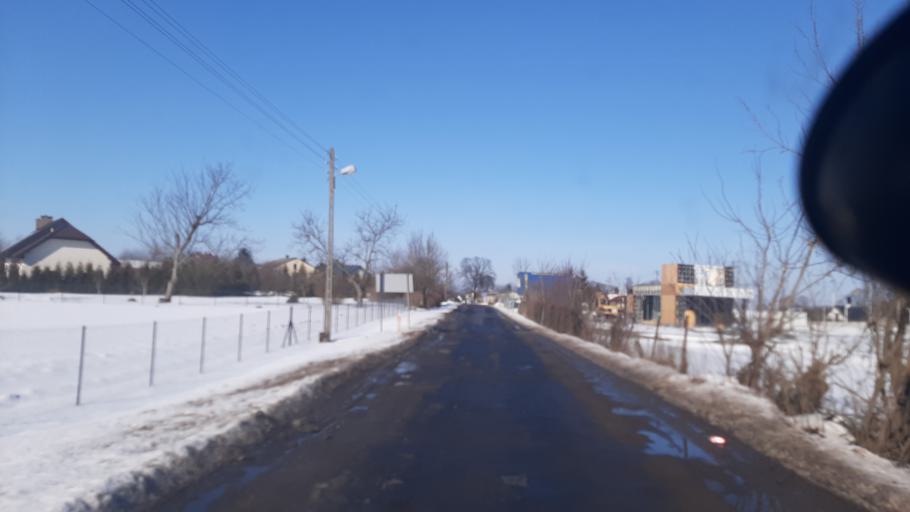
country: PL
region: Lublin Voivodeship
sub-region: Powiat lubelski
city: Wojciechow
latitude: 51.2858
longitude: 22.2838
